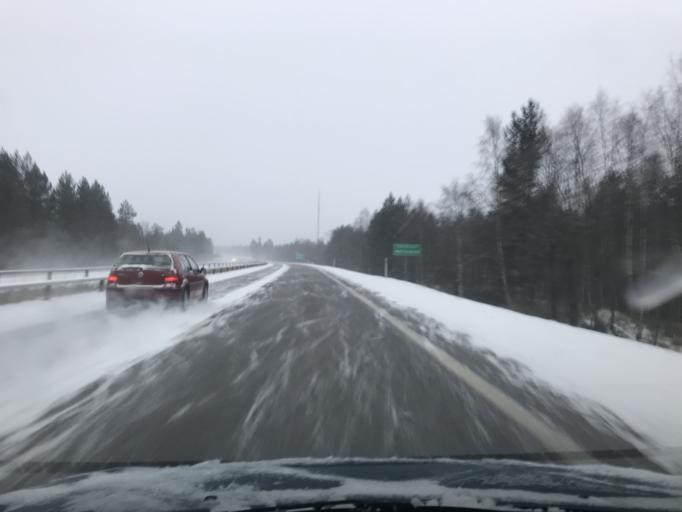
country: SE
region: Norrbotten
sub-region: Lulea Kommun
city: Gammelstad
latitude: 65.6289
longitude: 22.0451
